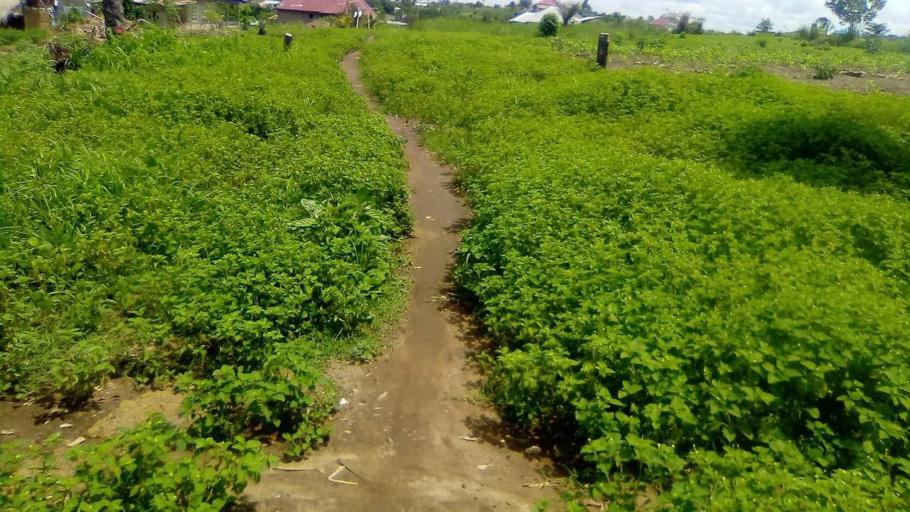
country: SL
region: Southern Province
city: Bo
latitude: 7.9354
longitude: -11.7466
